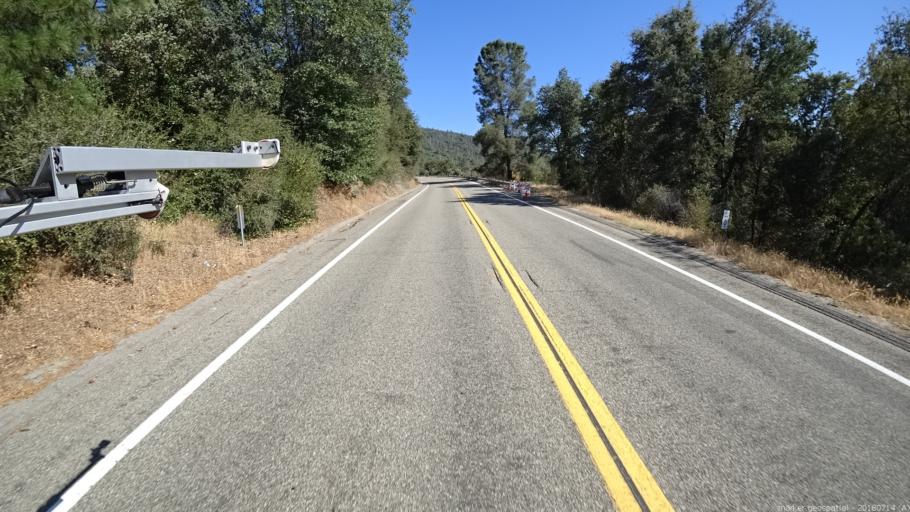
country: US
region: California
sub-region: Madera County
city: Oakhurst
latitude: 37.3862
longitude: -119.6314
